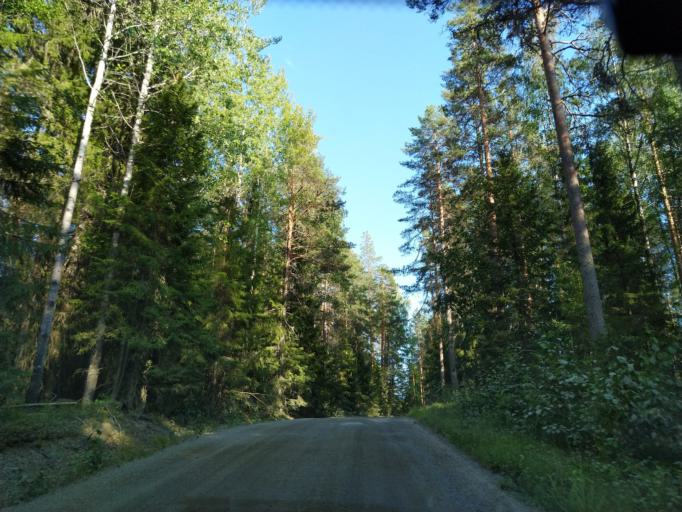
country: FI
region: Central Finland
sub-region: Jaemsae
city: Kuhmoinen
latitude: 61.6768
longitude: 24.9930
